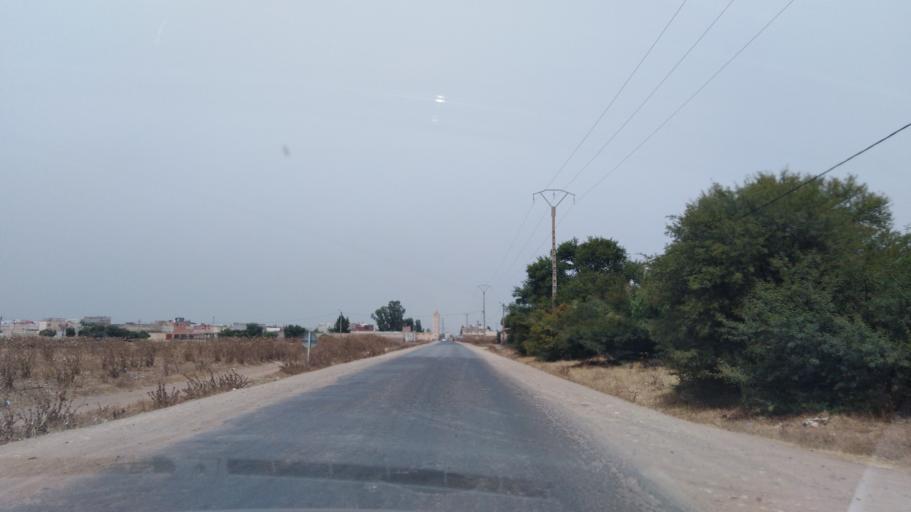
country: MA
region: Grand Casablanca
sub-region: Mediouna
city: Mediouna
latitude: 33.4125
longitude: -7.5154
